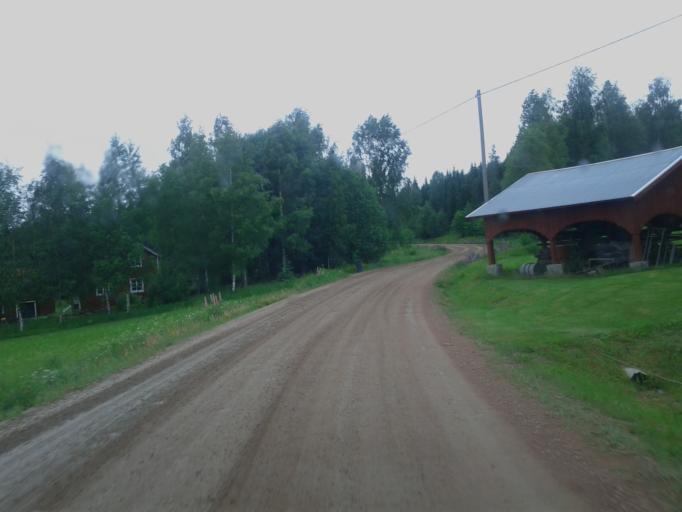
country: SE
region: Gaevleborg
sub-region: Hudiksvalls Kommun
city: Delsbo
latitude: 62.1484
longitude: 16.5954
